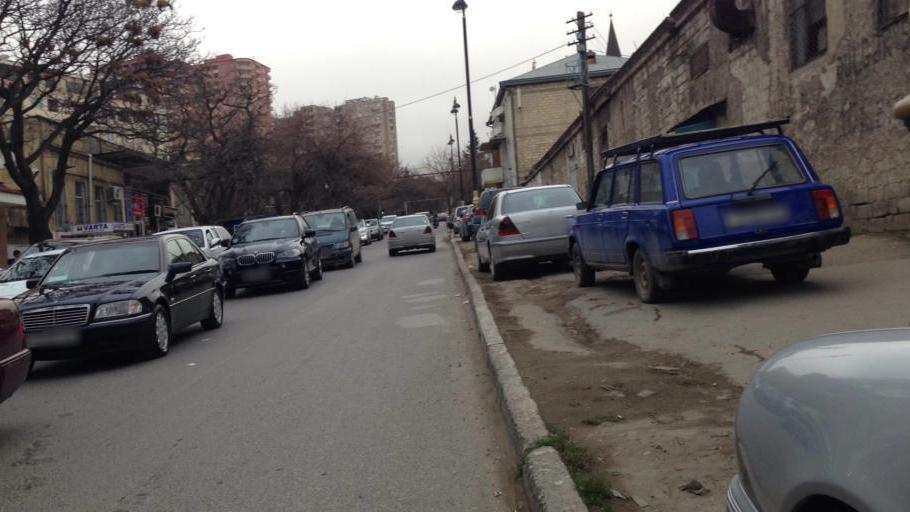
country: AZ
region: Baki
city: Baku
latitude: 40.3881
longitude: 49.8509
